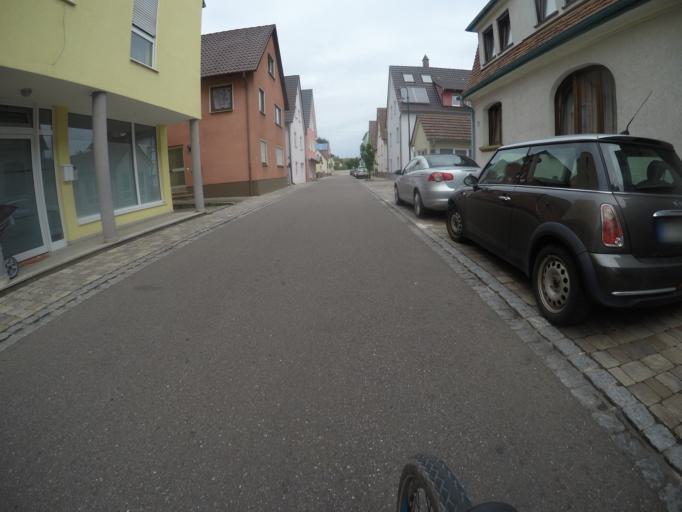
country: DE
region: Baden-Wuerttemberg
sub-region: Karlsruhe Region
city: Muhlacker
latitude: 48.9427
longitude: 8.8412
